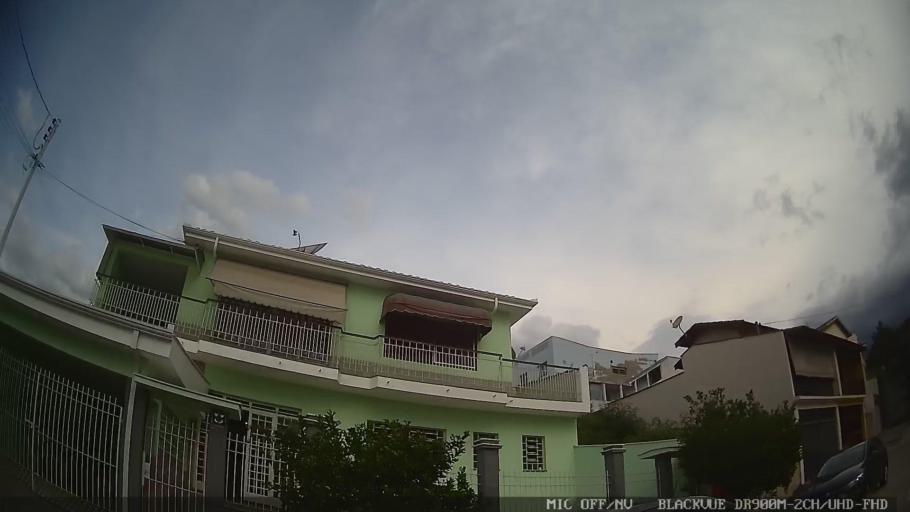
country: BR
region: Sao Paulo
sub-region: Amparo
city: Amparo
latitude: -22.7082
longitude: -46.7702
